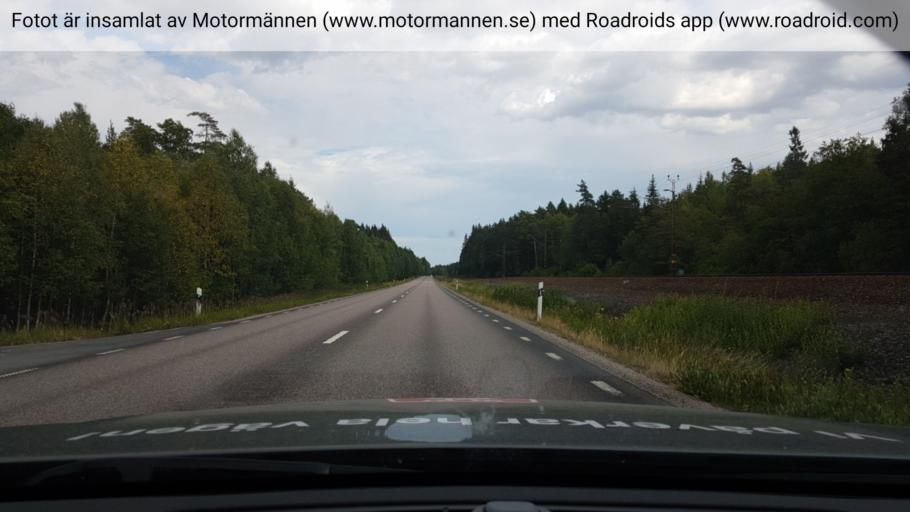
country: SE
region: Uppsala
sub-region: Enkopings Kommun
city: Orsundsbro
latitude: 59.8832
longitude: 17.2191
